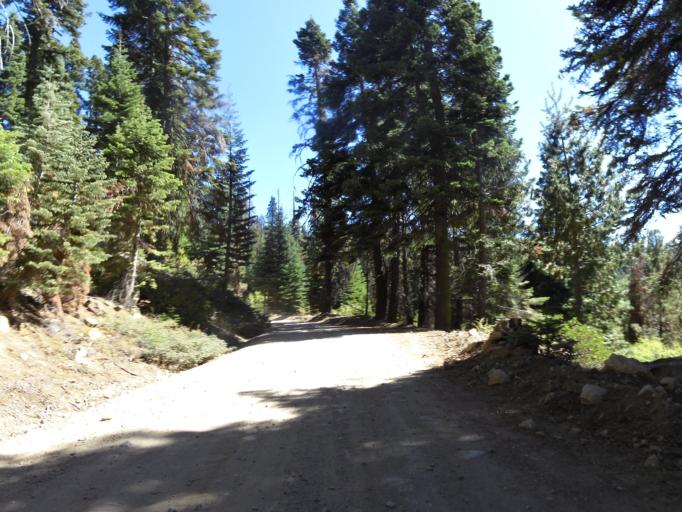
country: US
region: California
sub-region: Madera County
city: Oakhurst
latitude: 37.4375
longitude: -119.5098
